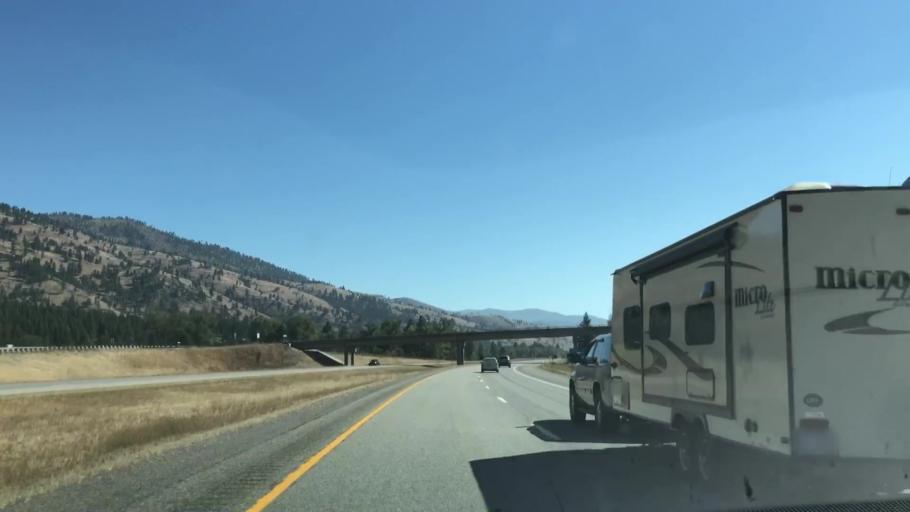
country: US
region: Montana
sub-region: Missoula County
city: Clinton
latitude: 46.7292
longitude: -113.6699
